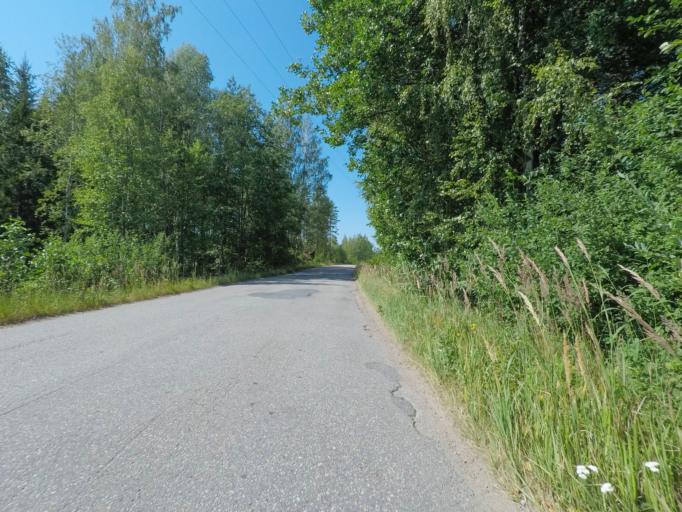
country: FI
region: Southern Savonia
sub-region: Mikkeli
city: Puumala
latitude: 61.4225
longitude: 28.1431
